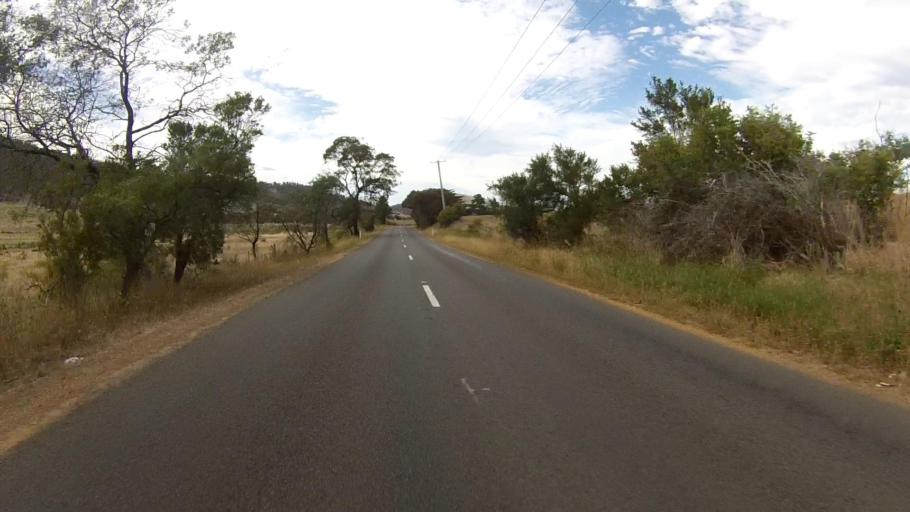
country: AU
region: Tasmania
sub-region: Clarence
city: Cambridge
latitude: -42.7186
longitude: 147.3875
